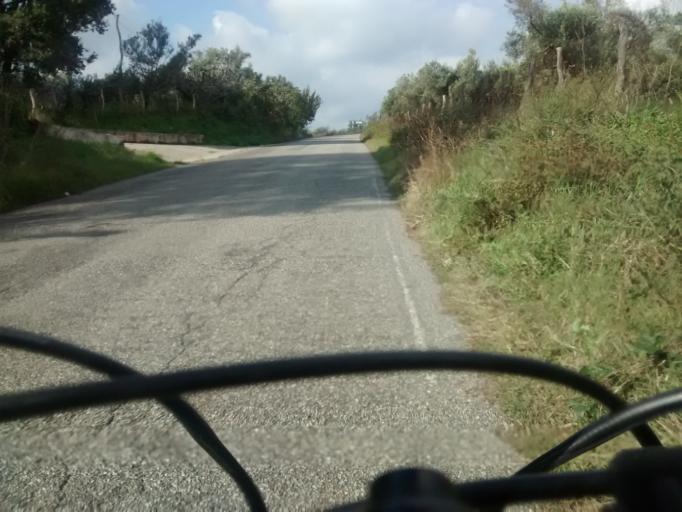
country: IT
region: Calabria
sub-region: Provincia di Catanzaro
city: Cortale
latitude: 38.8802
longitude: 16.4107
